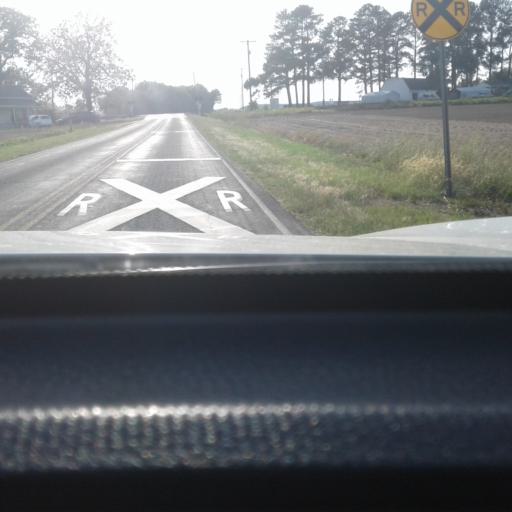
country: US
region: North Carolina
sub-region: Harnett County
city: Dunn
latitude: 35.3353
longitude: -78.5859
